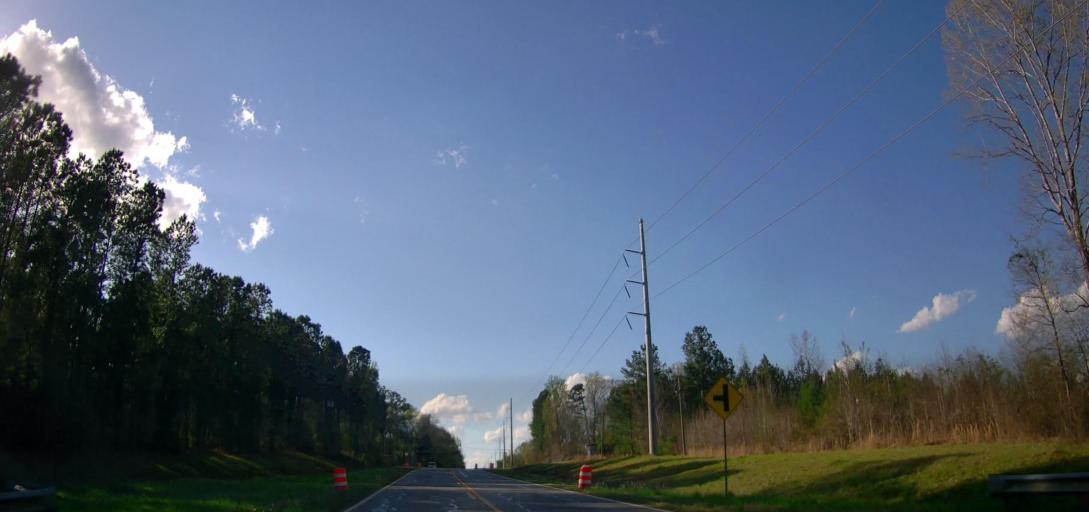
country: US
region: Georgia
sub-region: Baldwin County
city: Milledgeville
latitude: 33.1472
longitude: -83.3393
